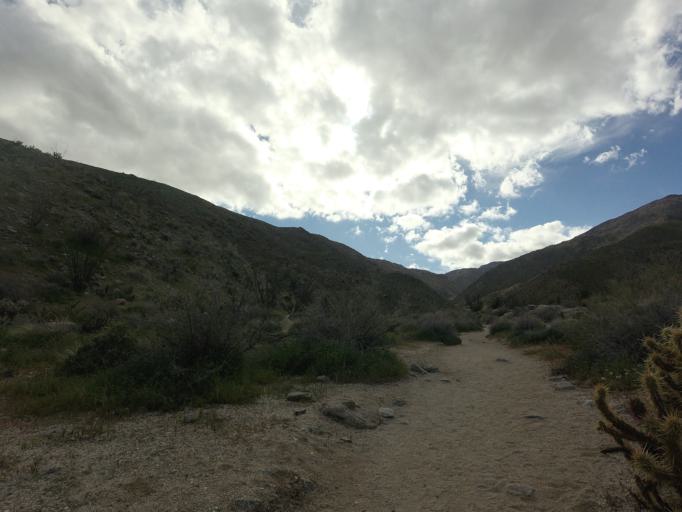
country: US
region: California
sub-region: San Diego County
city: Borrego Springs
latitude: 33.2434
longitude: -116.4217
